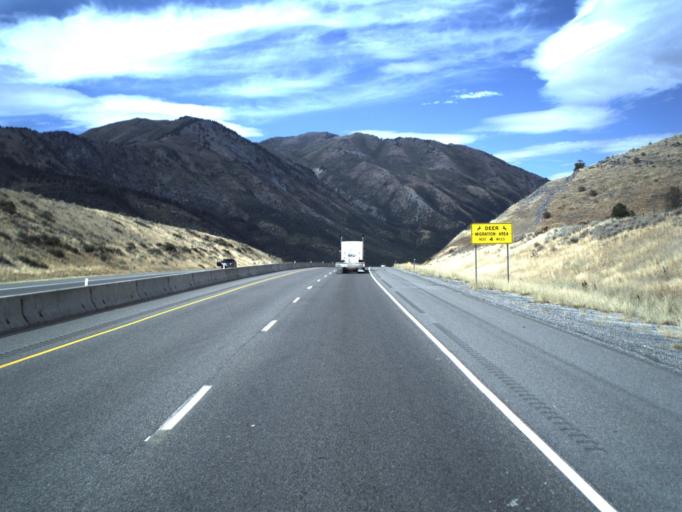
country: US
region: Utah
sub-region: Cache County
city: Wellsville
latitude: 41.5758
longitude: -111.9716
